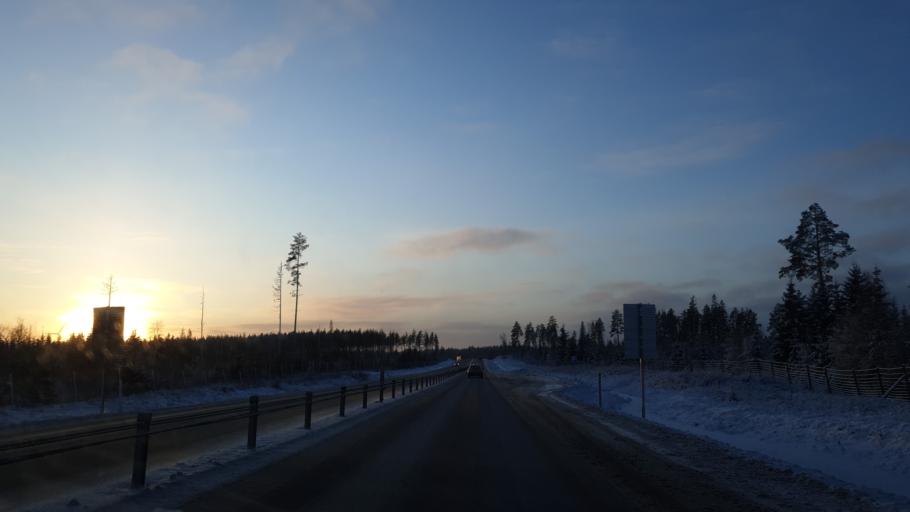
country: SE
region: Vaesterbotten
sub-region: Umea Kommun
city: Hoernefors
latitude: 63.6696
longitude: 19.9754
